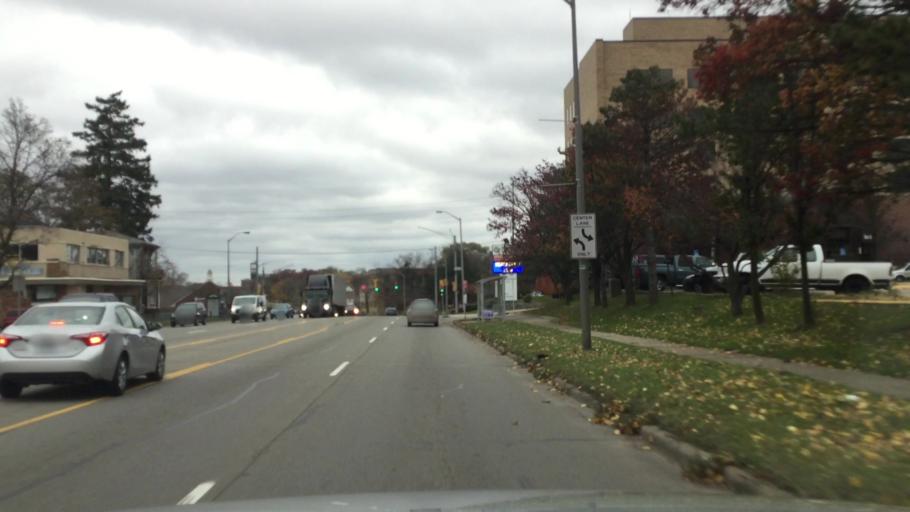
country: US
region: Michigan
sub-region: Oakland County
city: Pontiac
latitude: 42.6356
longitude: -83.3109
